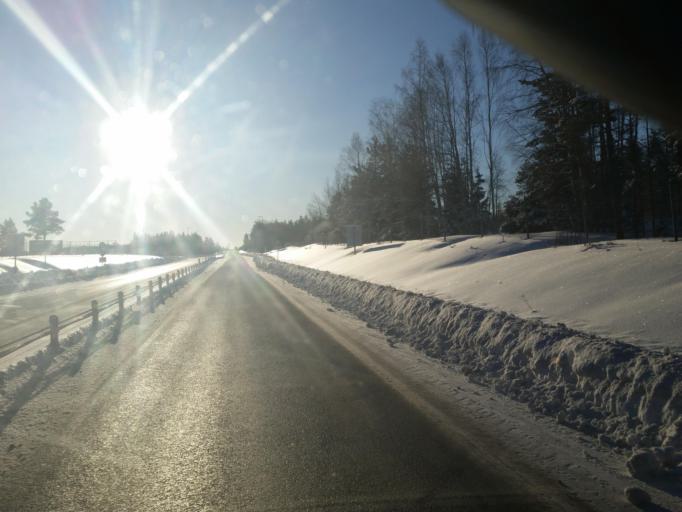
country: SE
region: Norrbotten
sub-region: Pitea Kommun
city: Pitea
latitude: 65.2313
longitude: 21.5052
